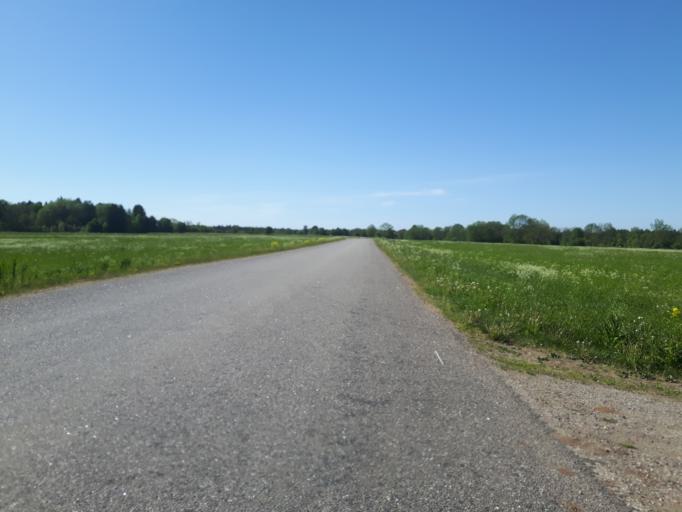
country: EE
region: Laeaene-Virumaa
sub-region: Haljala vald
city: Haljala
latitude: 59.5436
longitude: 26.2173
